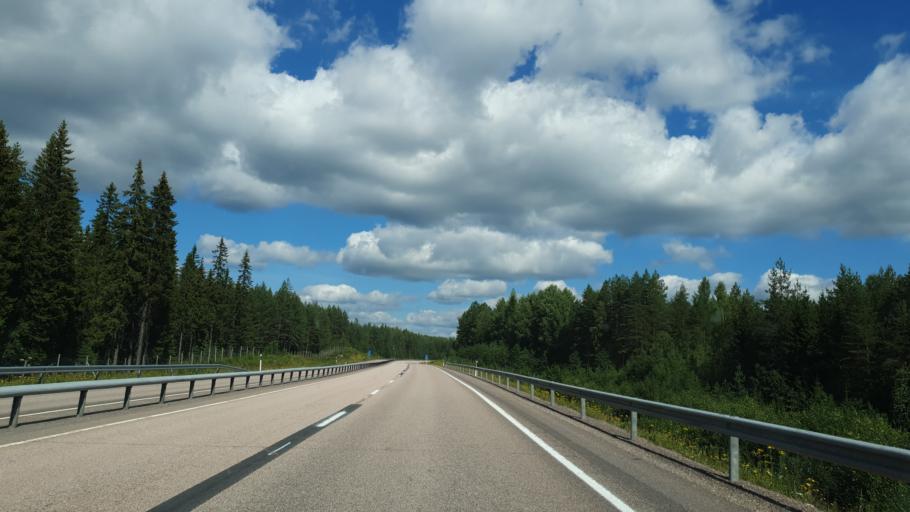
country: FI
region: Central Finland
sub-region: Jaemsae
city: Jaemsae
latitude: 61.8132
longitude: 25.0058
